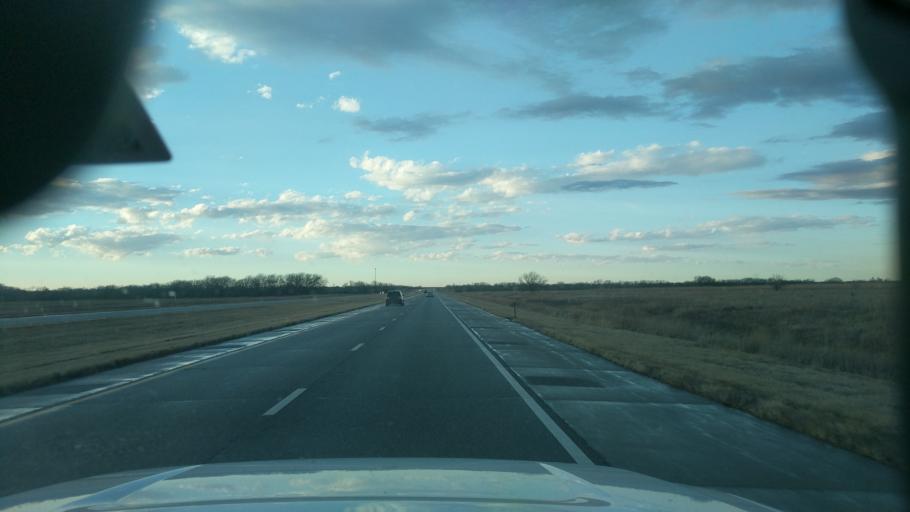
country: US
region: Kansas
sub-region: Harvey County
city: Hesston
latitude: 38.1794
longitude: -97.4547
